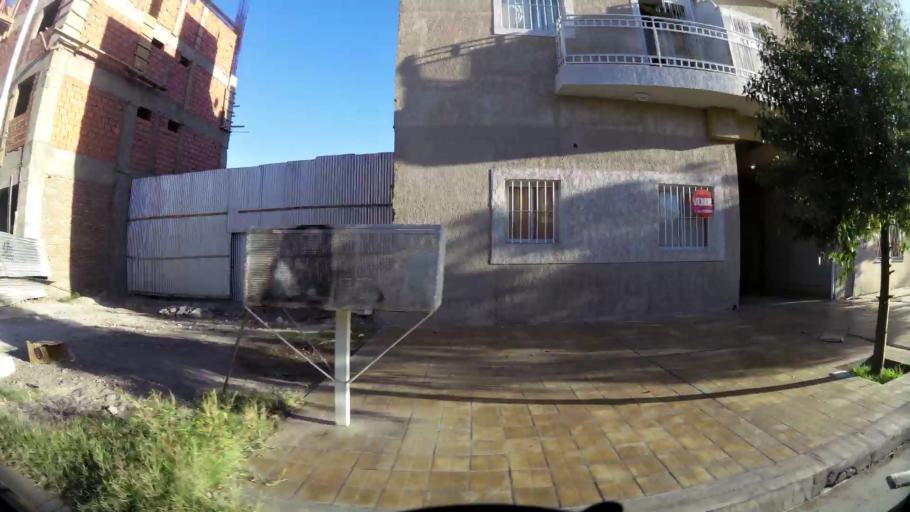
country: AR
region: San Juan
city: San Juan
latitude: -31.5450
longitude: -68.5227
